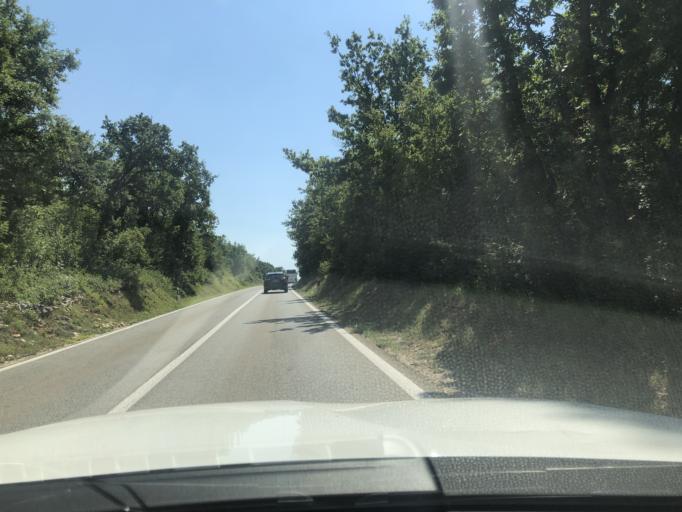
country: HR
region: Istarska
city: Vodnjan
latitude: 45.0219
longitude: 13.8019
